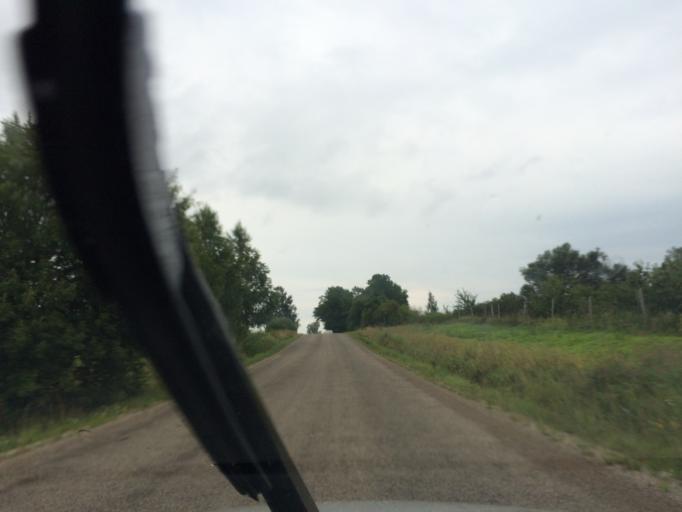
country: LV
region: Rezekne
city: Rezekne
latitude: 56.5630
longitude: 27.4474
